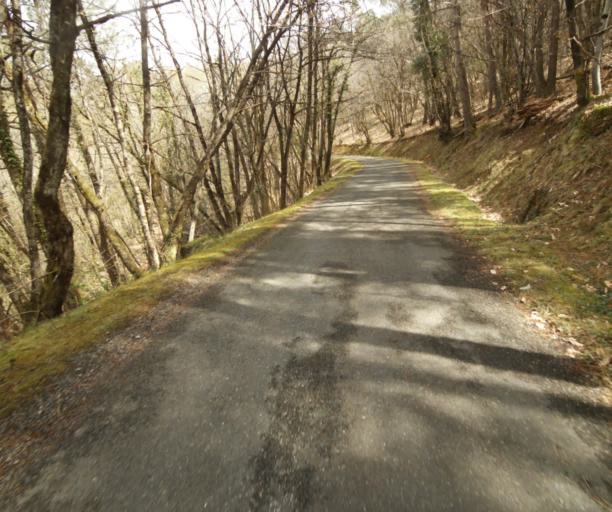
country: FR
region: Limousin
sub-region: Departement de la Correze
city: Sainte-Fortunade
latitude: 45.1827
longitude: 1.8694
